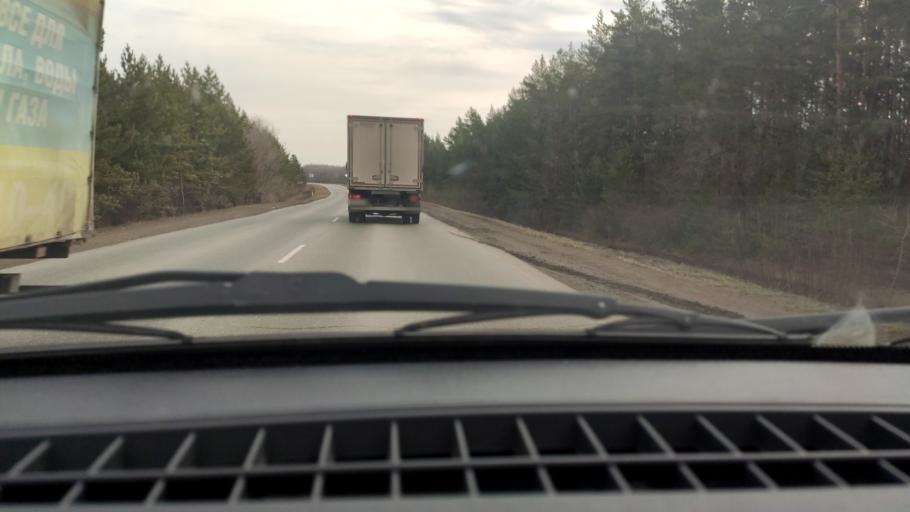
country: RU
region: Bashkortostan
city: Davlekanovo
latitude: 54.2449
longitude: 55.0738
